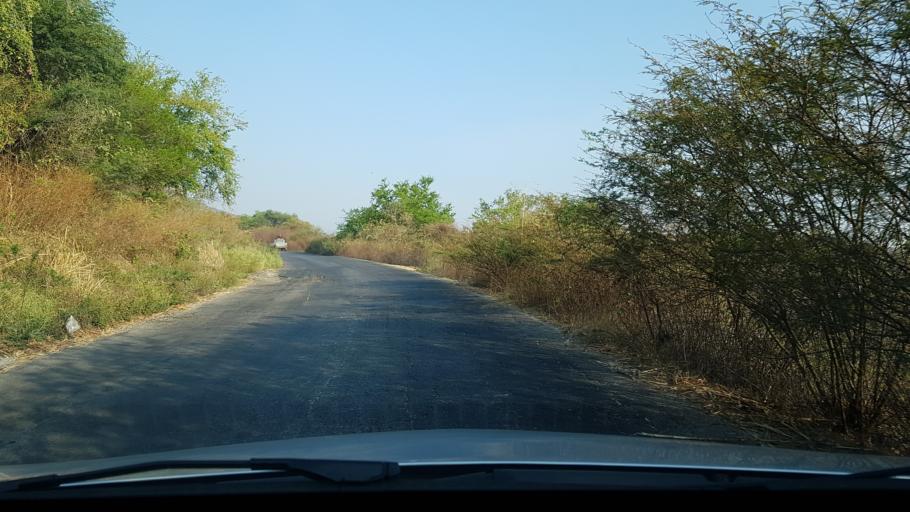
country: MX
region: Morelos
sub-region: Tepalcingo
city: Zacapalco
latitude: 18.6514
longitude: -99.0301
